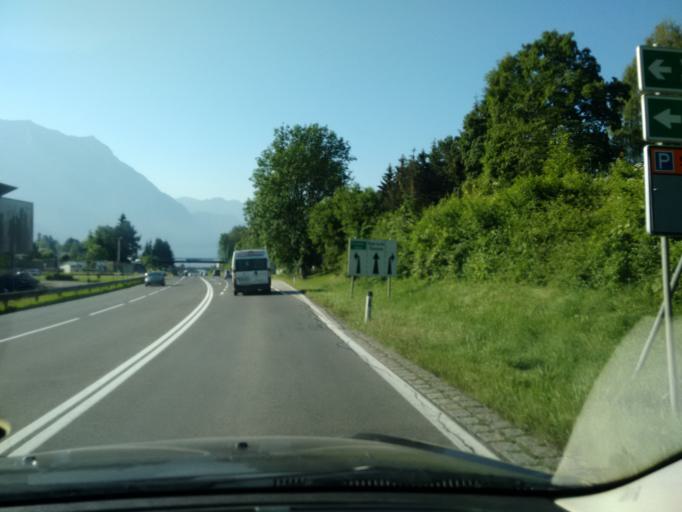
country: AT
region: Upper Austria
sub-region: Politischer Bezirk Gmunden
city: Altmunster
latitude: 47.9141
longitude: 13.7769
